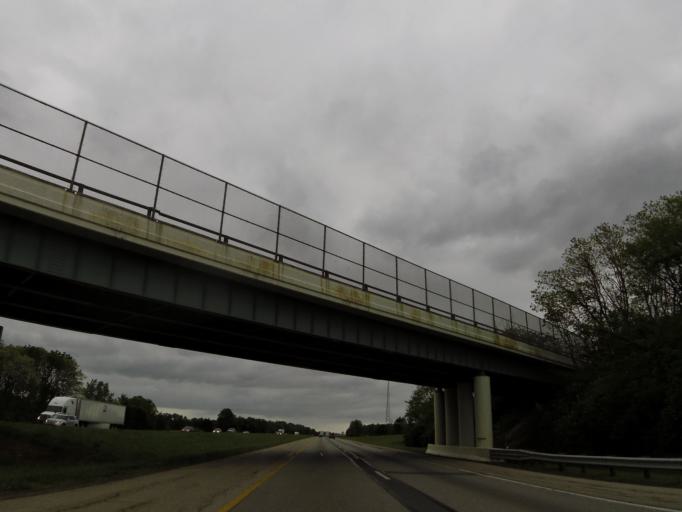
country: US
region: Ohio
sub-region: Warren County
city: Morrow
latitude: 39.4295
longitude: -84.0796
